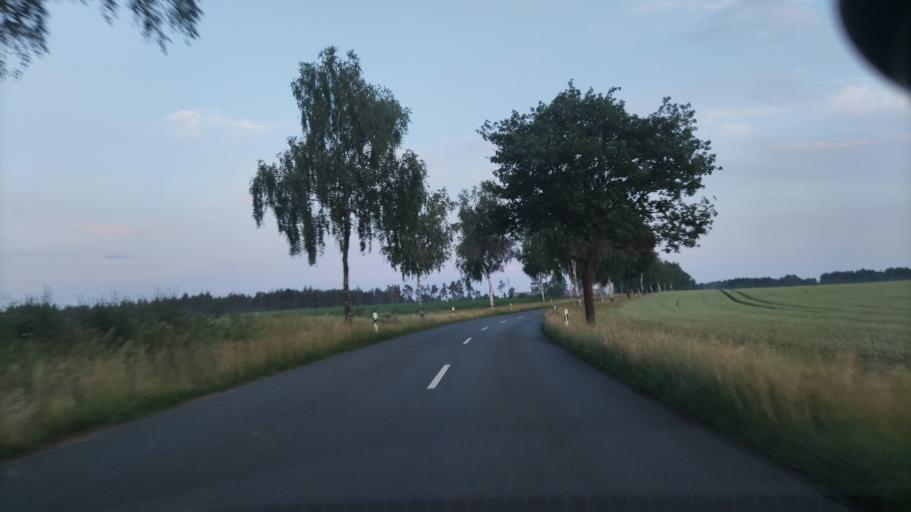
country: DE
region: Lower Saxony
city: Bispingen
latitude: 53.1170
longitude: 10.0571
